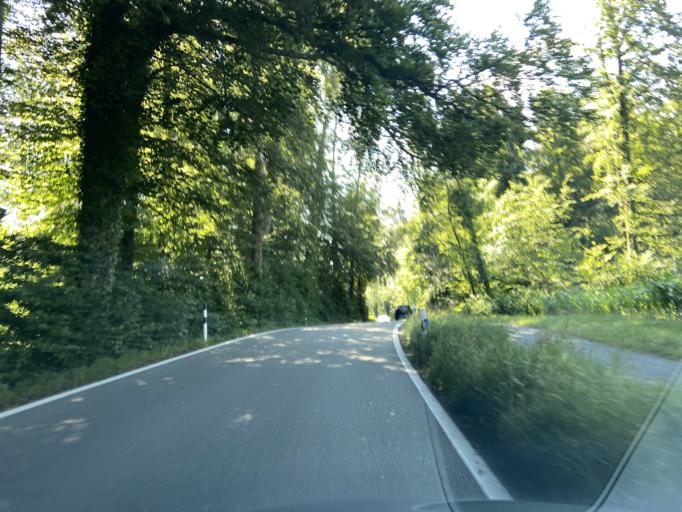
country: CH
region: Zurich
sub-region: Bezirk Meilen
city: Oetwil am See
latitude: 47.2605
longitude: 8.7182
